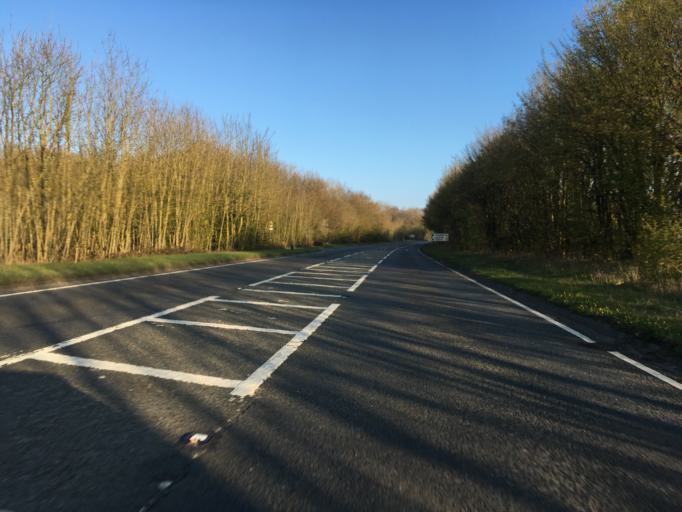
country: GB
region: England
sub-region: Gloucestershire
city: Westfield
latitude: 51.8498
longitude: -1.8881
